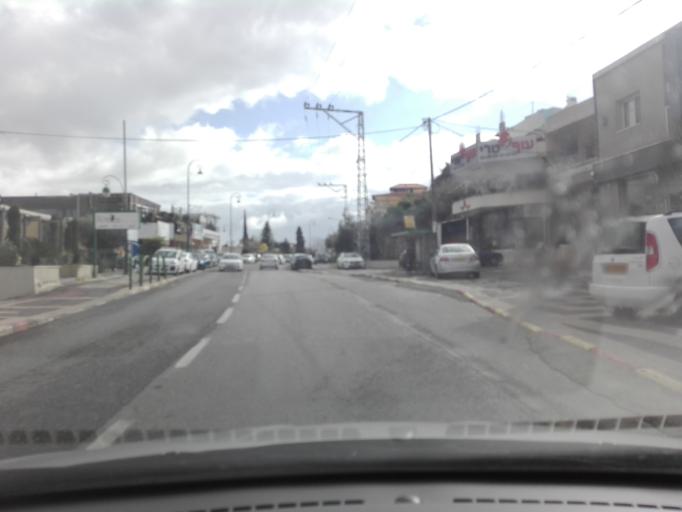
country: IL
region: Haifa
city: Daliyat el Karmil
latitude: 32.7231
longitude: 35.0590
